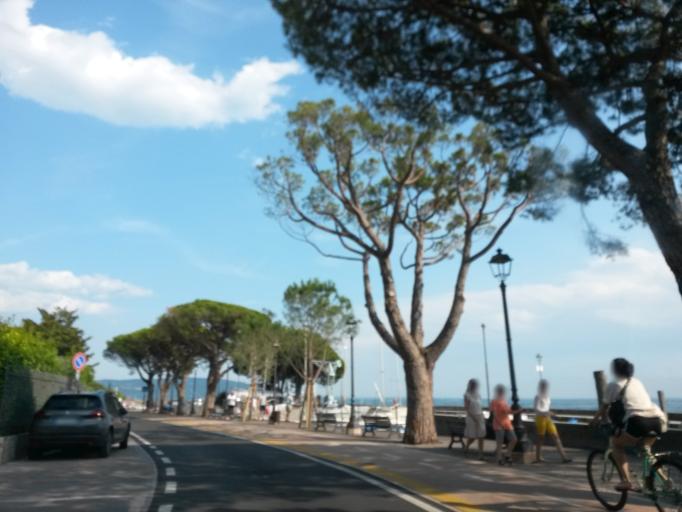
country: IT
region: Lombardy
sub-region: Provincia di Brescia
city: Toscolano Maderno
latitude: 45.6335
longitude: 10.5998
